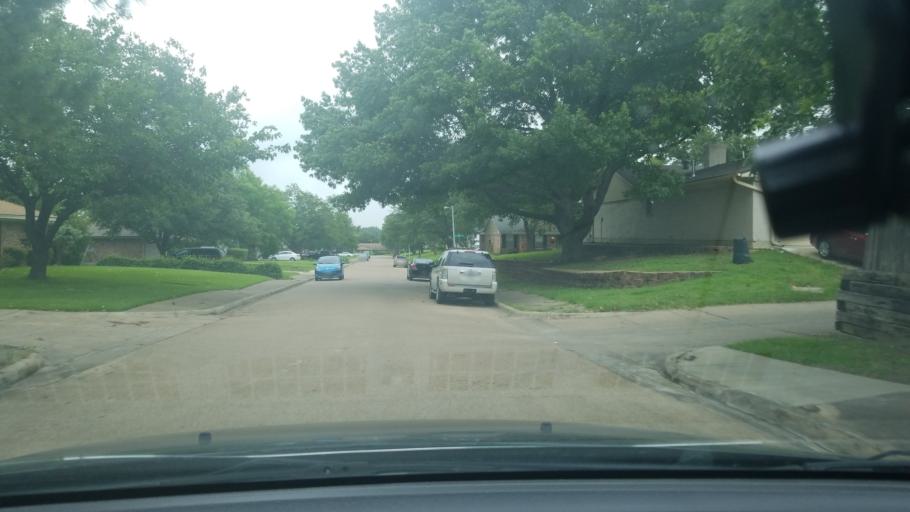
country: US
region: Texas
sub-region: Dallas County
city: Mesquite
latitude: 32.7803
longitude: -96.6345
